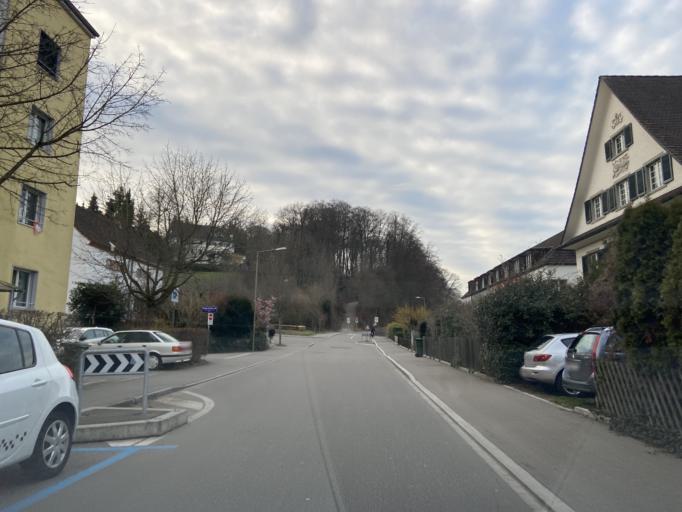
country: CH
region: Zurich
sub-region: Bezirk Winterthur
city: Stadt Winterthur (Kreis 1) / Neuwiesen
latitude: 47.4988
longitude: 8.7159
